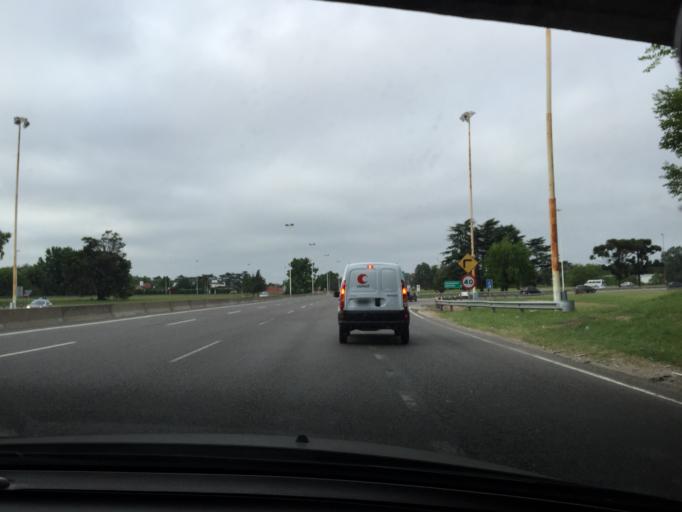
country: AR
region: Buenos Aires
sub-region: Partido de Ezeiza
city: Ezeiza
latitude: -34.7839
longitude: -58.5250
